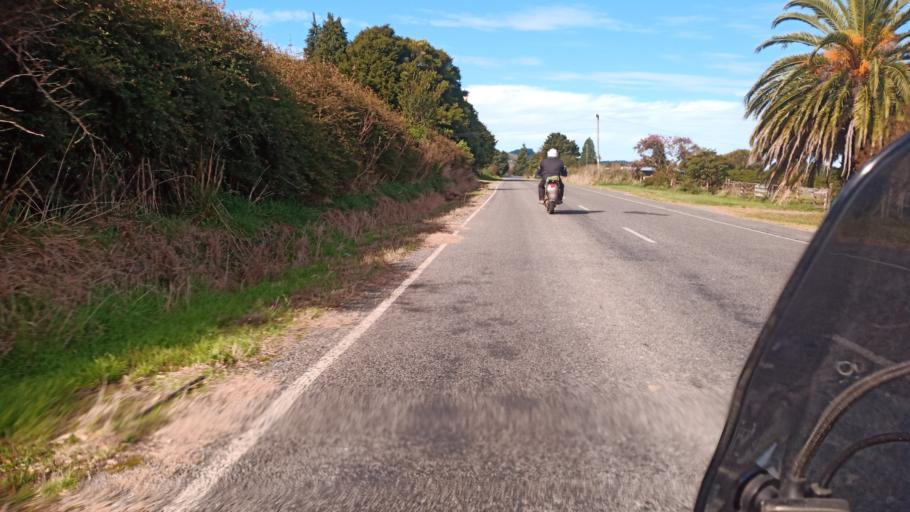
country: NZ
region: Hawke's Bay
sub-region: Wairoa District
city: Wairoa
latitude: -39.0706
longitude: 177.1433
